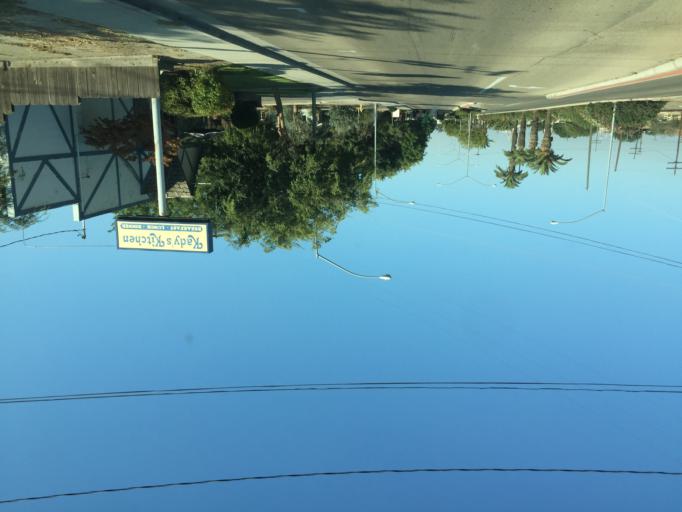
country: US
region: California
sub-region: Fresno County
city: Kingsburg
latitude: 36.5163
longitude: -119.5573
